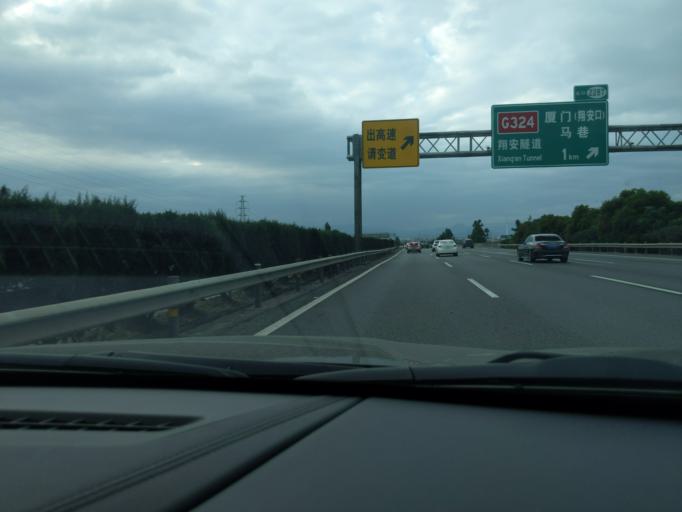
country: CN
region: Fujian
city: Maxiang
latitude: 24.6889
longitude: 118.2483
